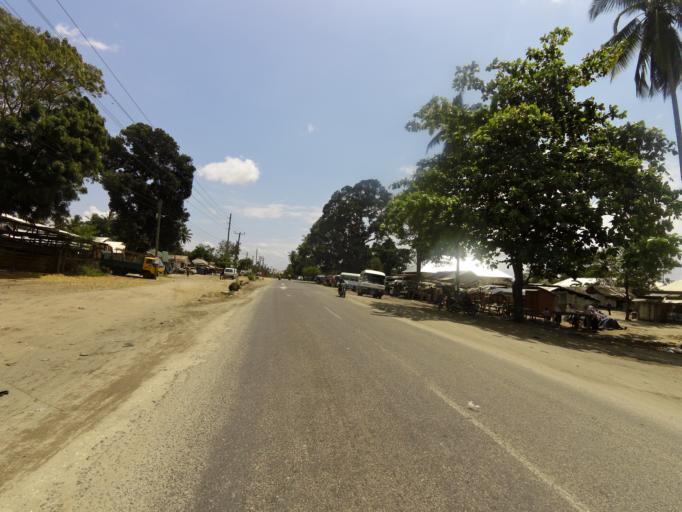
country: TZ
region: Pwani
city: Vikindu
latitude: -7.0332
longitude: 39.2824
